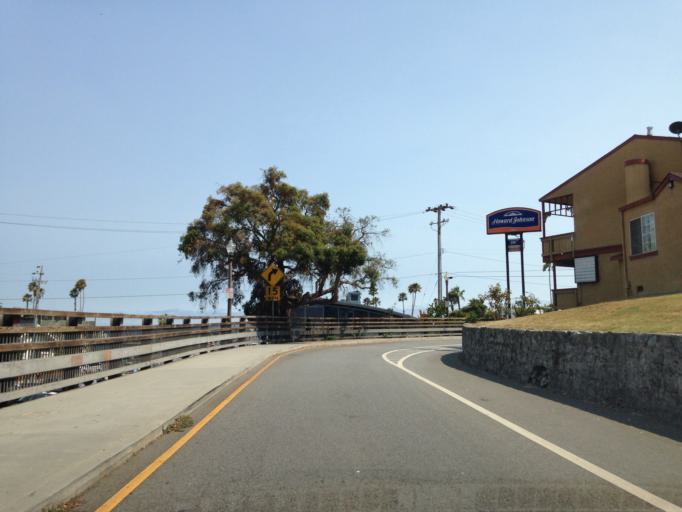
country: US
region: California
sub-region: Santa Cruz County
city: Santa Cruz
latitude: 36.9639
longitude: -122.0252
